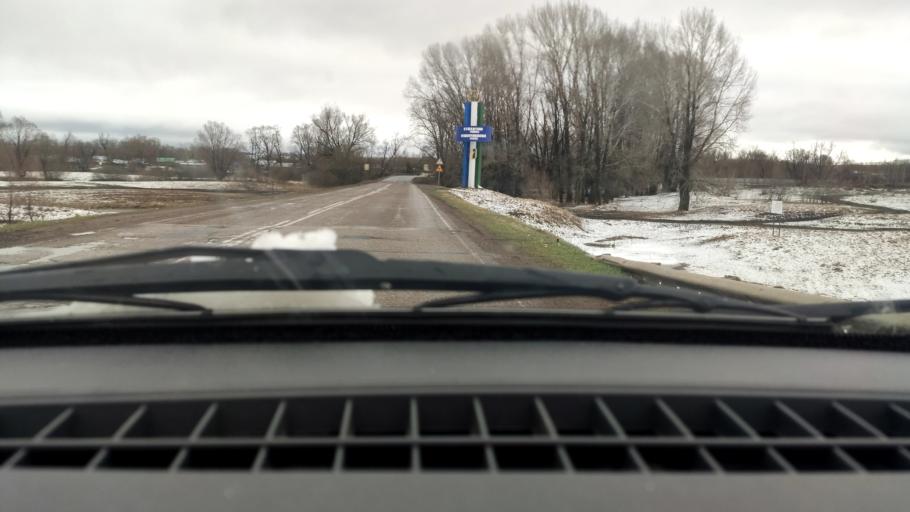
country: RU
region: Bashkortostan
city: Alekseyevka
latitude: 55.0769
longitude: 55.0742
